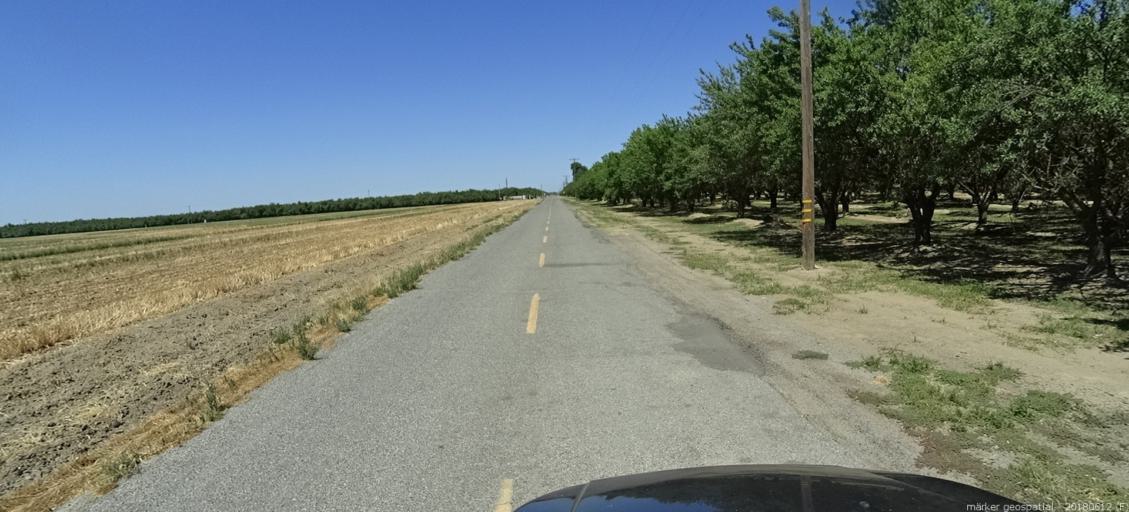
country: US
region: California
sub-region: Madera County
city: Chowchilla
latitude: 37.0470
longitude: -120.3799
